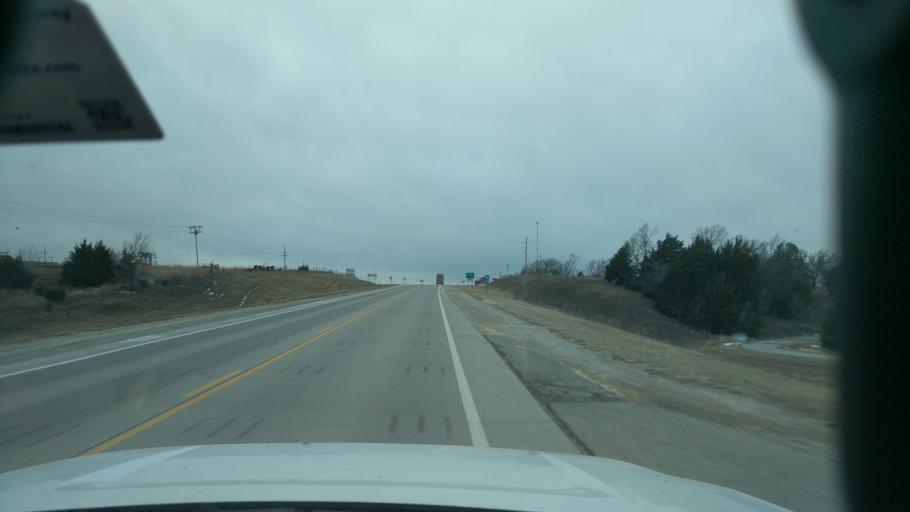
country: US
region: Kansas
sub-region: Marion County
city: Marion
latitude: 38.3628
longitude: -97.0371
